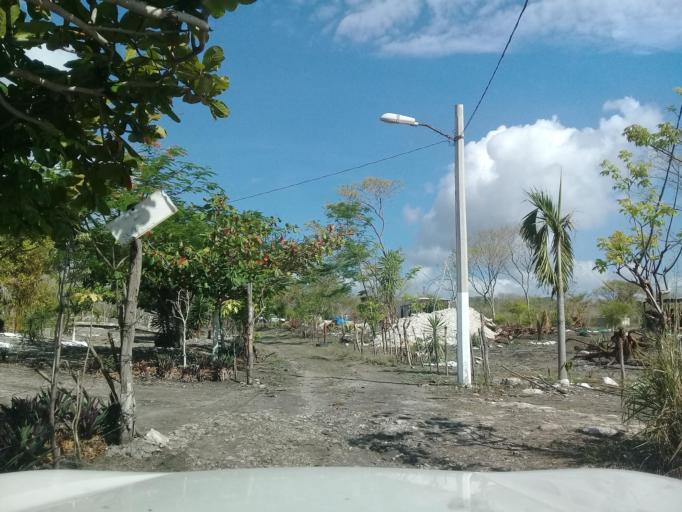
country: MX
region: Veracruz
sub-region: Emiliano Zapata
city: Plan del Rio
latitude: 19.4113
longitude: -96.6531
